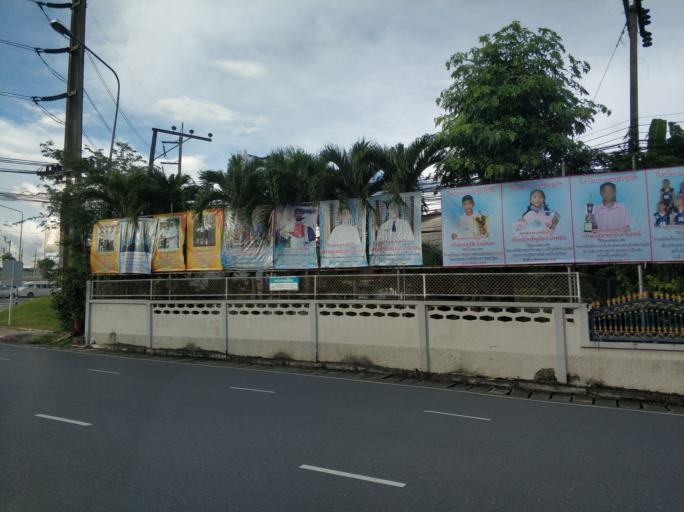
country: TH
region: Phuket
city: Wichit
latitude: 7.8891
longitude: 98.3685
